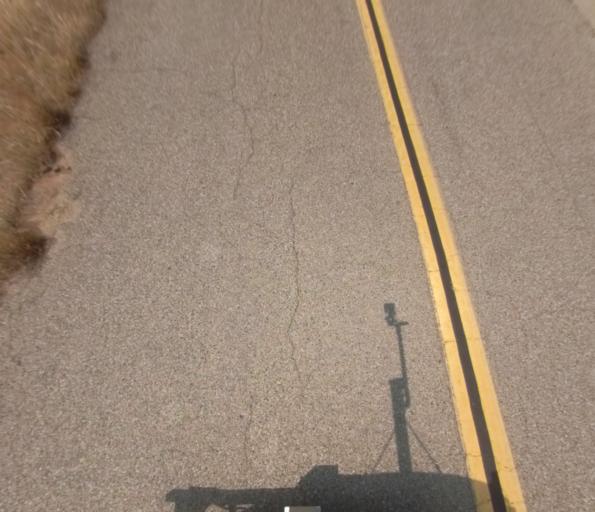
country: US
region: California
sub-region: Madera County
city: Yosemite Lakes
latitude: 37.2835
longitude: -119.8170
